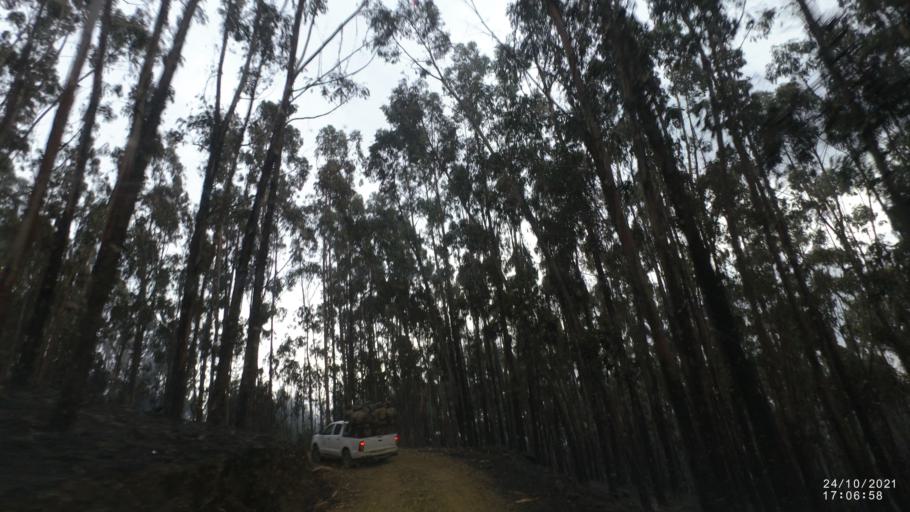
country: BO
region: Cochabamba
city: Cochabamba
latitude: -17.3325
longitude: -66.1397
